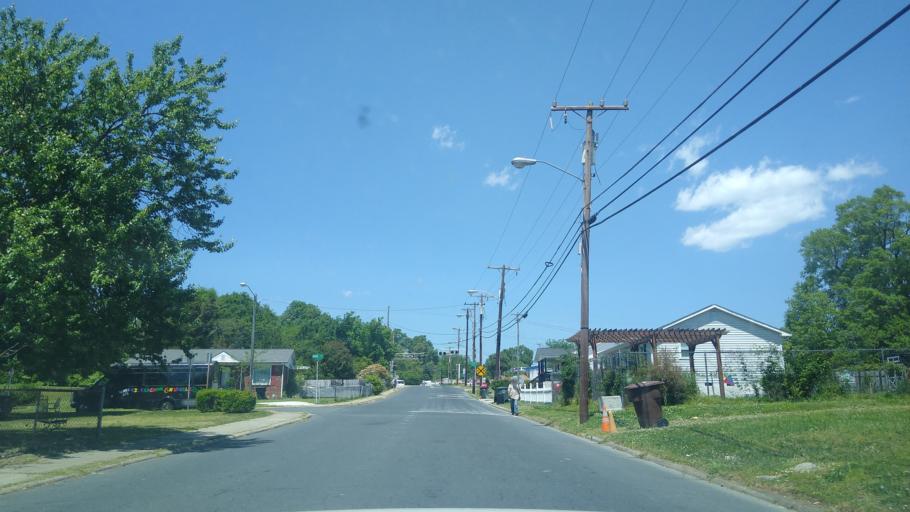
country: US
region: North Carolina
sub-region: Guilford County
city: Greensboro
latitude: 36.0720
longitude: -79.7641
